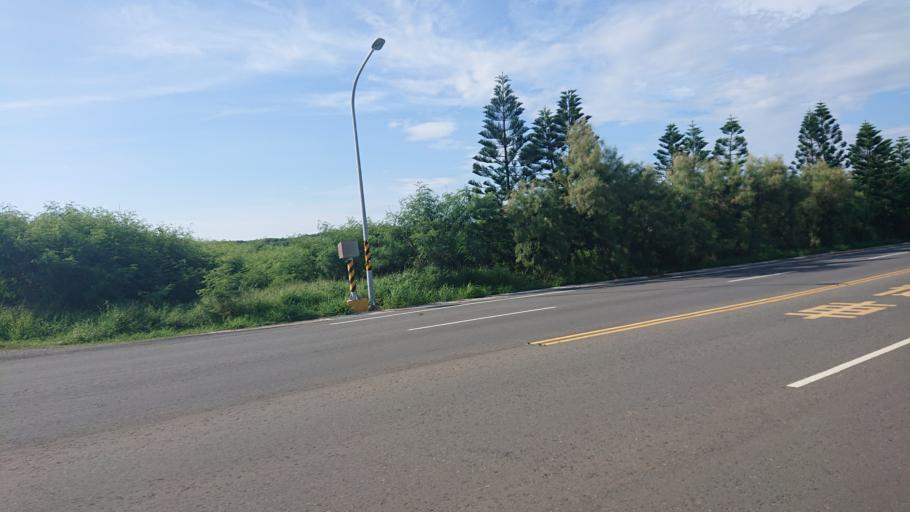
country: TW
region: Taiwan
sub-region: Penghu
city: Ma-kung
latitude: 23.5240
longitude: 119.5848
